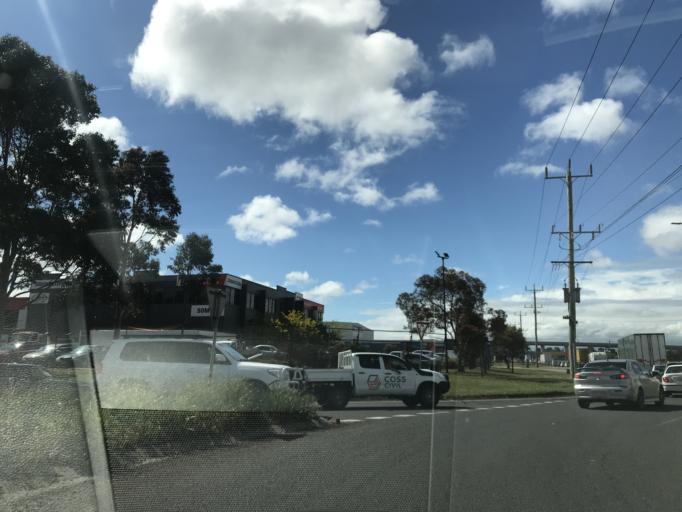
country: AU
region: Victoria
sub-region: Brimbank
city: Derrimut
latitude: -37.8056
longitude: 144.7880
